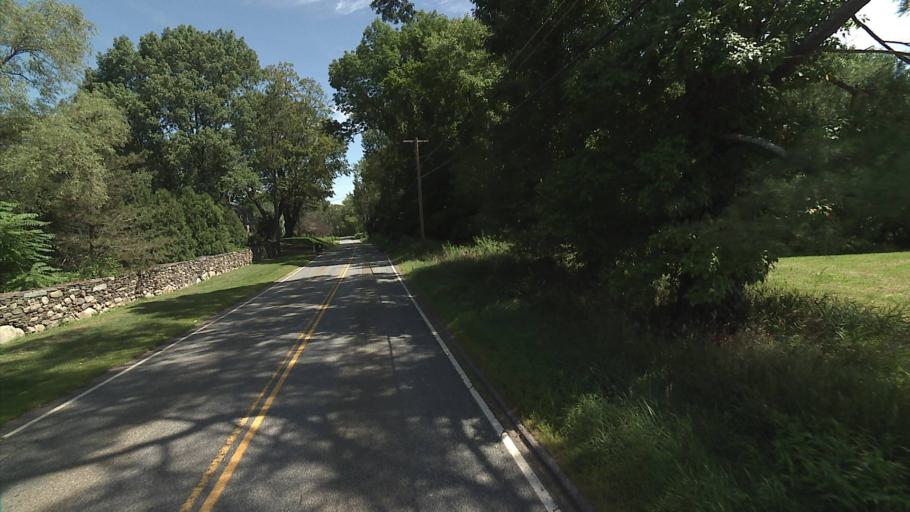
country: US
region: Connecticut
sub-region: Windham County
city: South Woodstock
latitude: 41.8710
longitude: -72.0017
